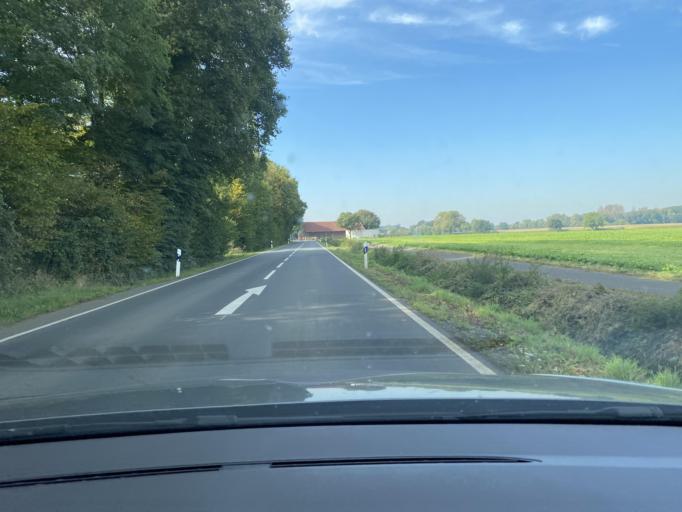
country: DE
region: North Rhine-Westphalia
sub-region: Regierungsbezirk Munster
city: Havixbeck
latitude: 51.9453
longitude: 7.4775
